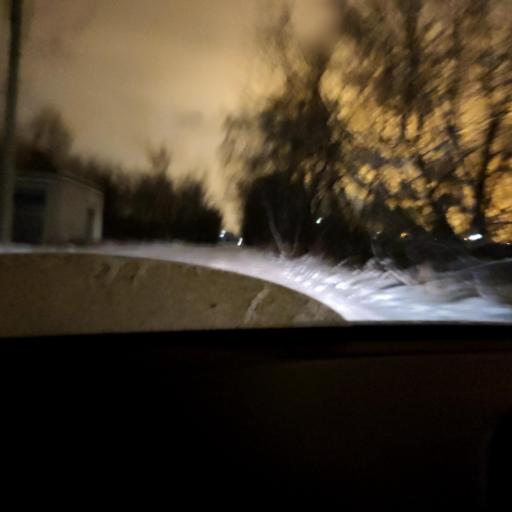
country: RU
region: Tatarstan
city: Staroye Arakchino
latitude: 55.8609
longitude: 48.9775
